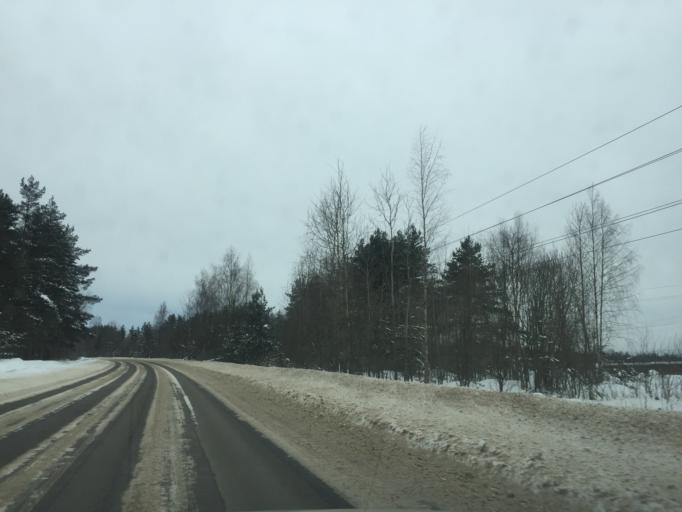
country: RU
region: Leningrad
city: Koltushi
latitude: 59.8716
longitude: 30.6718
